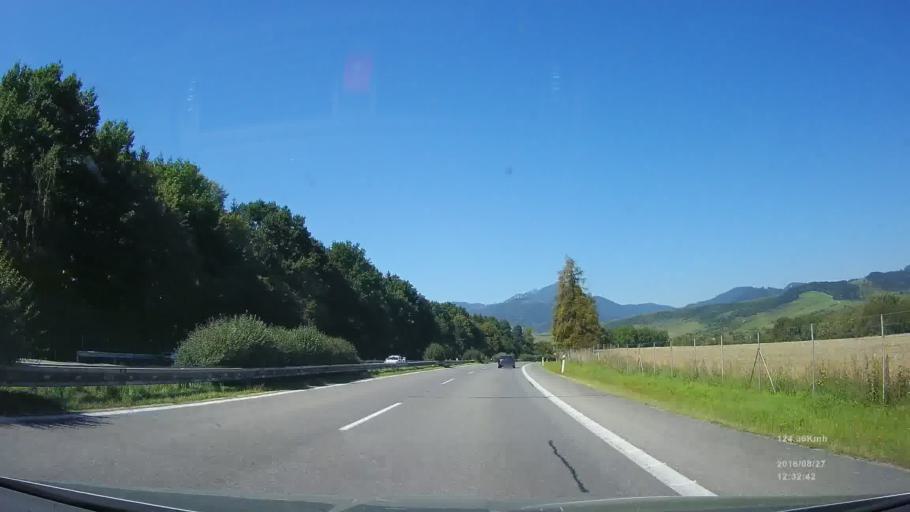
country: SK
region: Zilinsky
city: Ruzomberok
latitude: 49.0915
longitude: 19.4492
